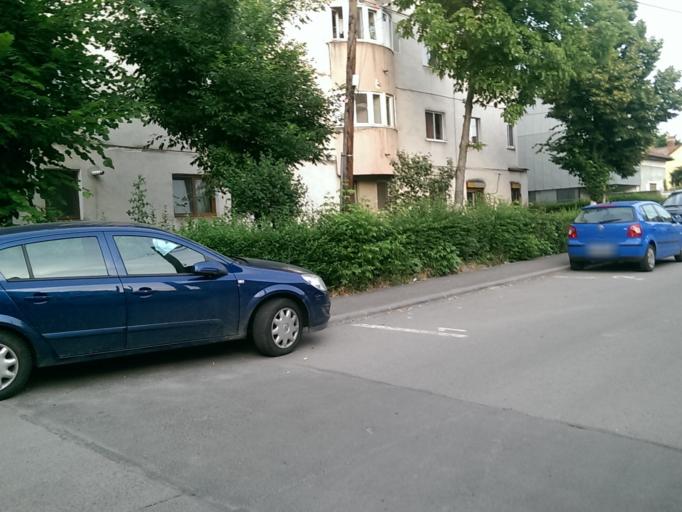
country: RO
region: Cluj
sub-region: Municipiul Cluj-Napoca
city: Cluj-Napoca
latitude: 46.7680
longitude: 23.6054
